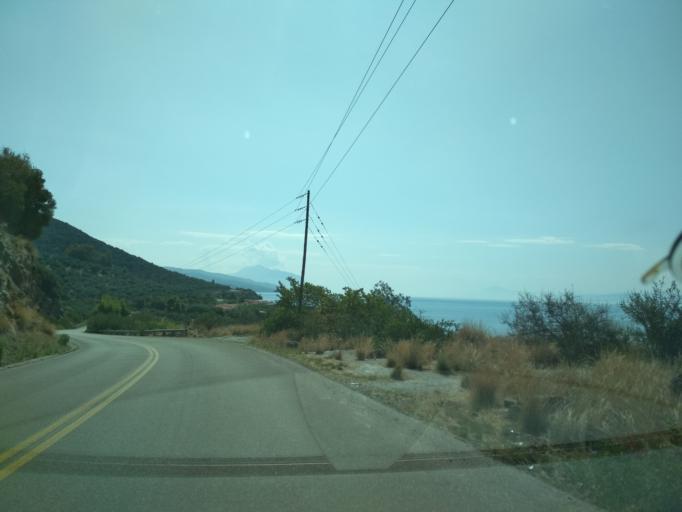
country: GR
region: Central Greece
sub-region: Nomos Evvoias
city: Roviai
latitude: 38.8445
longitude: 23.1658
